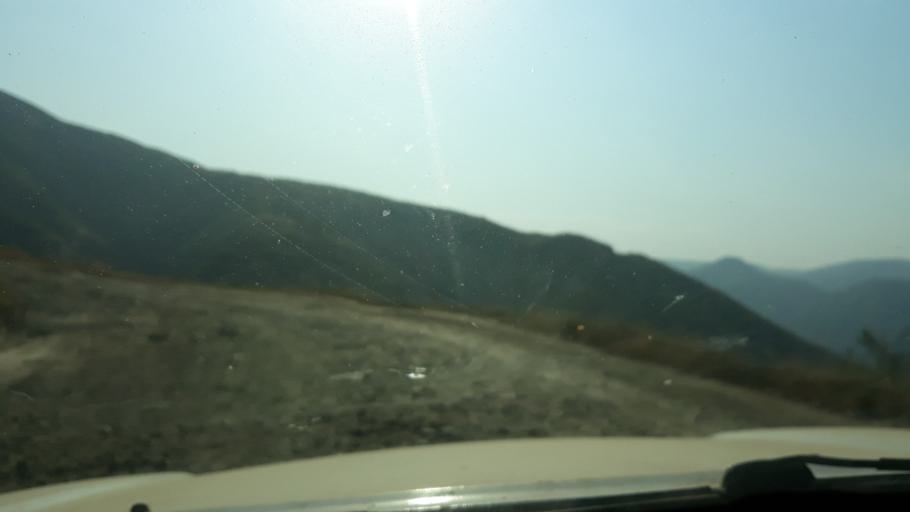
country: BI
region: Cibitoke
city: Cibitoke
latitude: -2.7099
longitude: 28.9952
